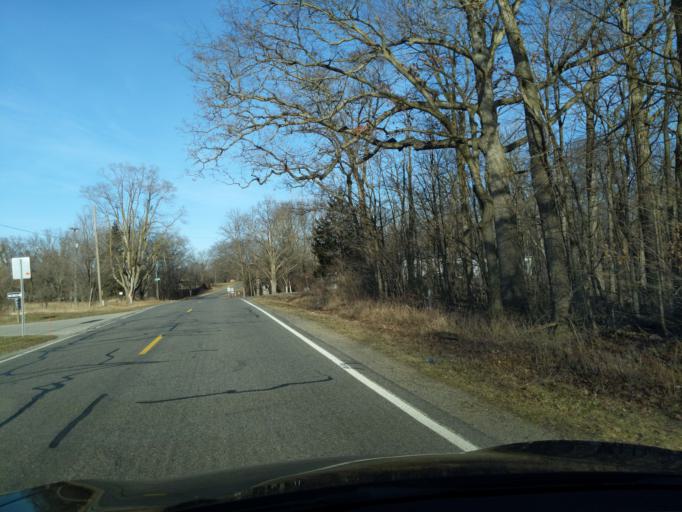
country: US
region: Michigan
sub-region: Ionia County
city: Saranac
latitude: 42.9346
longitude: -85.1951
